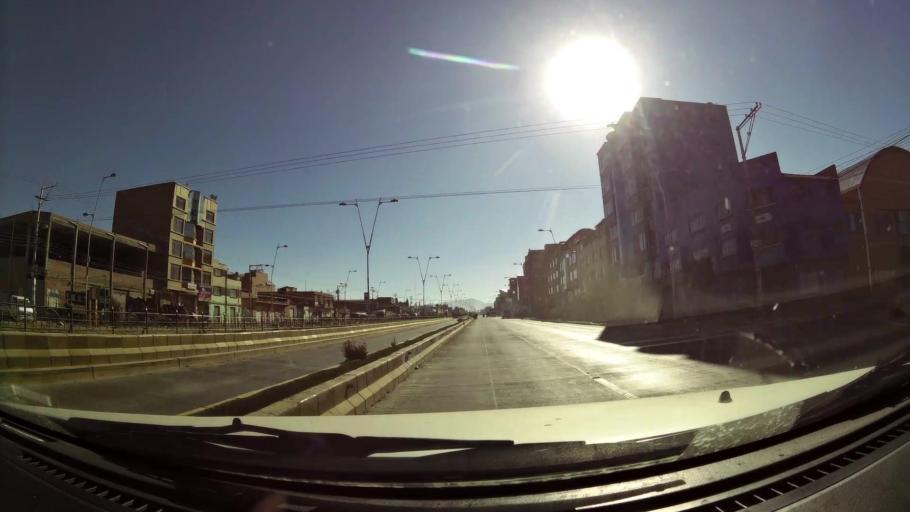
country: BO
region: La Paz
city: La Paz
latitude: -16.5248
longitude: -68.1816
